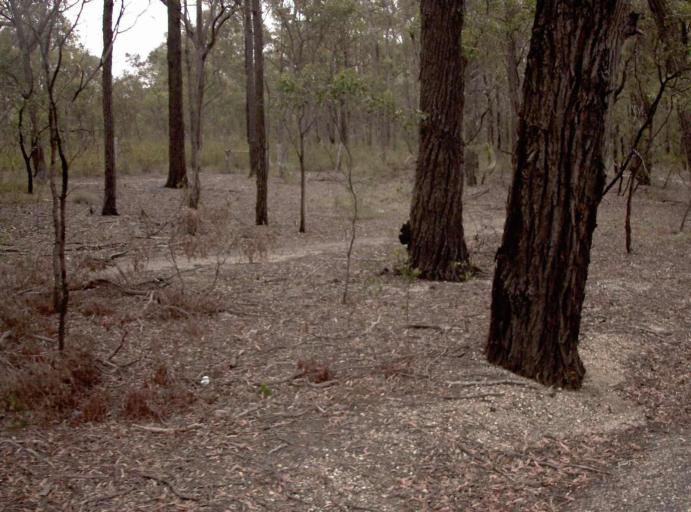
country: AU
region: Victoria
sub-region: Wellington
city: Heyfield
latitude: -37.9461
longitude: 146.7657
